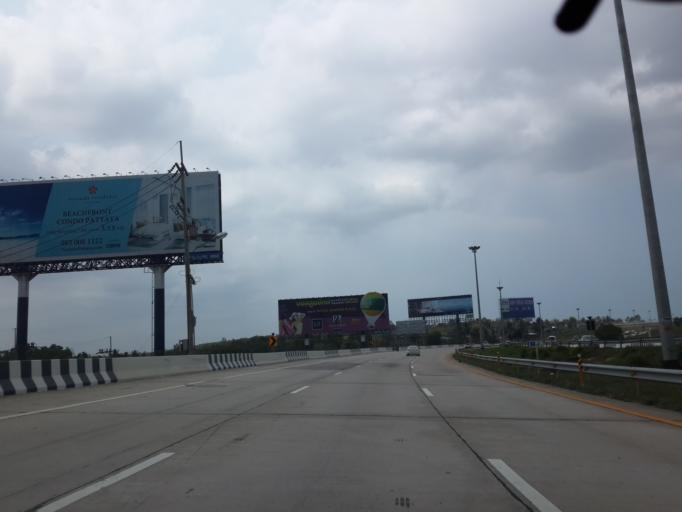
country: TH
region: Chon Buri
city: Phatthaya
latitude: 12.9538
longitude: 100.9720
